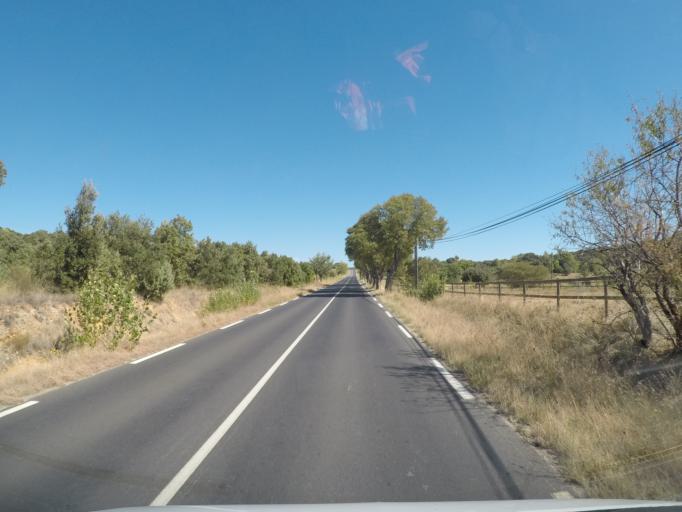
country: FR
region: Languedoc-Roussillon
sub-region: Departement de l'Herault
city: Aniane
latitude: 43.7038
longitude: 3.5959
